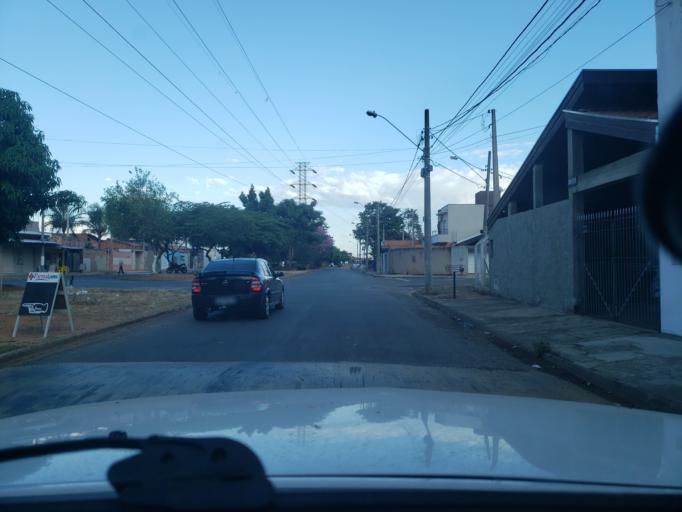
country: BR
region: Sao Paulo
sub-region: Moji-Guacu
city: Mogi-Gaucu
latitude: -22.3263
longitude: -46.9214
